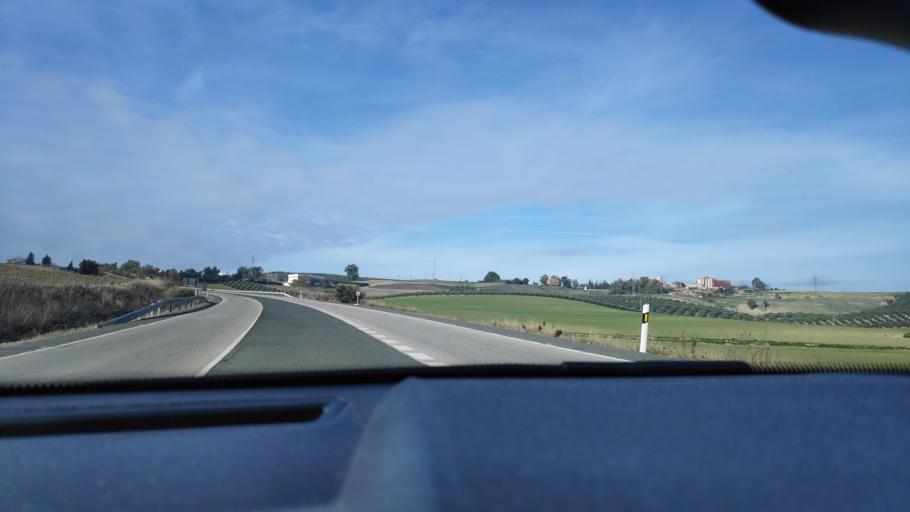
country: ES
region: Andalusia
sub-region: Provincia de Jaen
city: Linares
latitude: 38.0797
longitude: -3.6029
